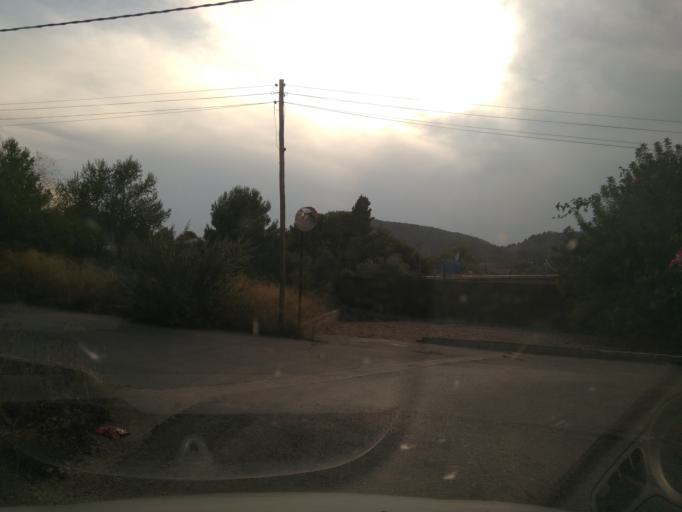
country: ES
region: Valencia
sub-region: Provincia de Valencia
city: Ribarroja
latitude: 39.5458
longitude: -0.5861
